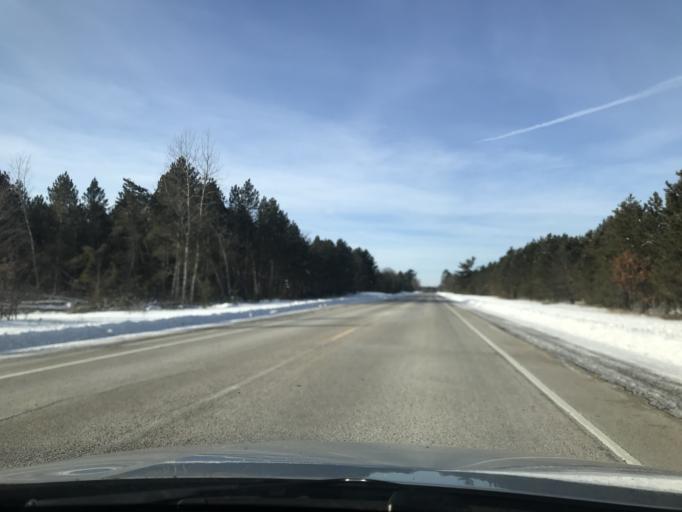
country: US
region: Wisconsin
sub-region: Oconto County
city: Gillett
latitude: 45.1199
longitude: -88.3883
